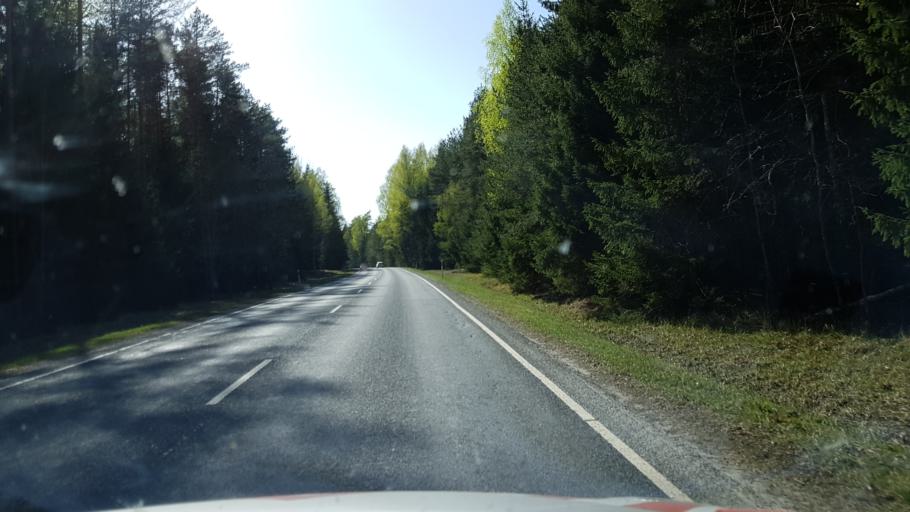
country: EE
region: Viljandimaa
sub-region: Moisakuela linn
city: Moisakula
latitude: 58.2574
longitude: 25.2133
